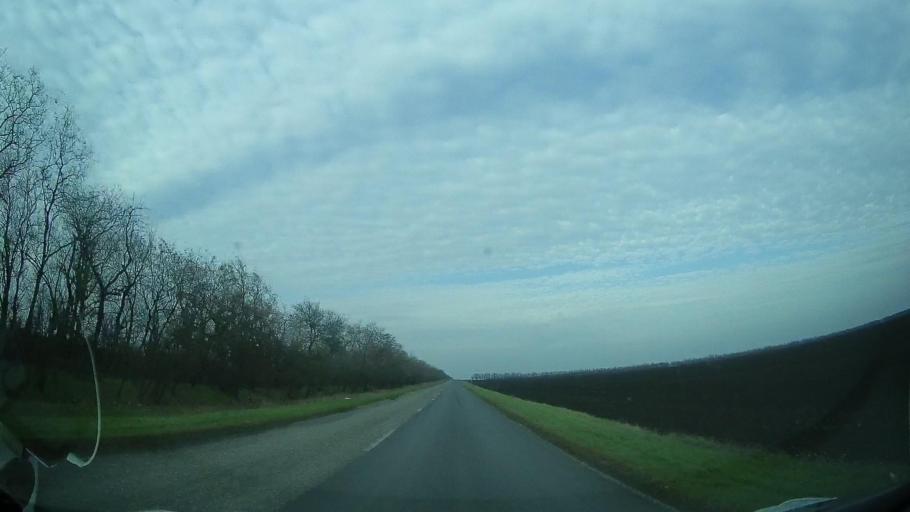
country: RU
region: Rostov
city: Zernograd
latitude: 46.9318
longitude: 40.3665
